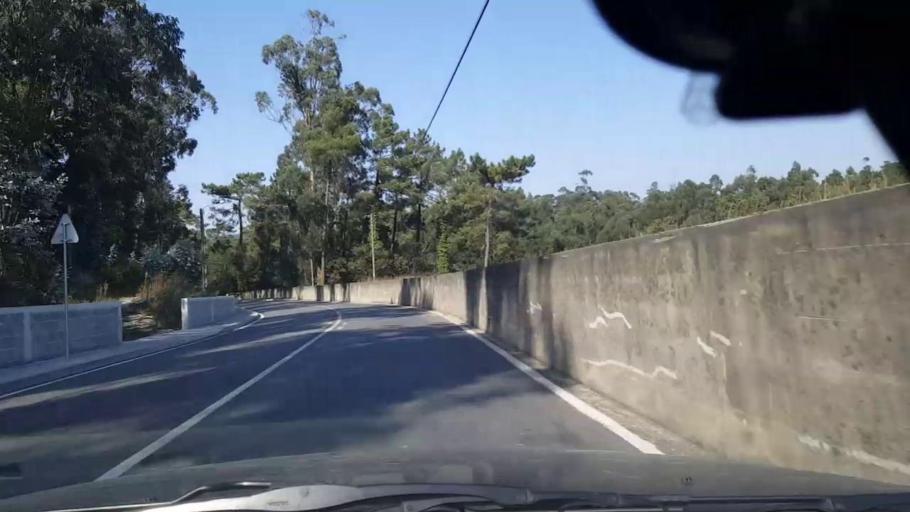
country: PT
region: Porto
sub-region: Vila do Conde
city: Arvore
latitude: 41.3875
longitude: -8.6863
